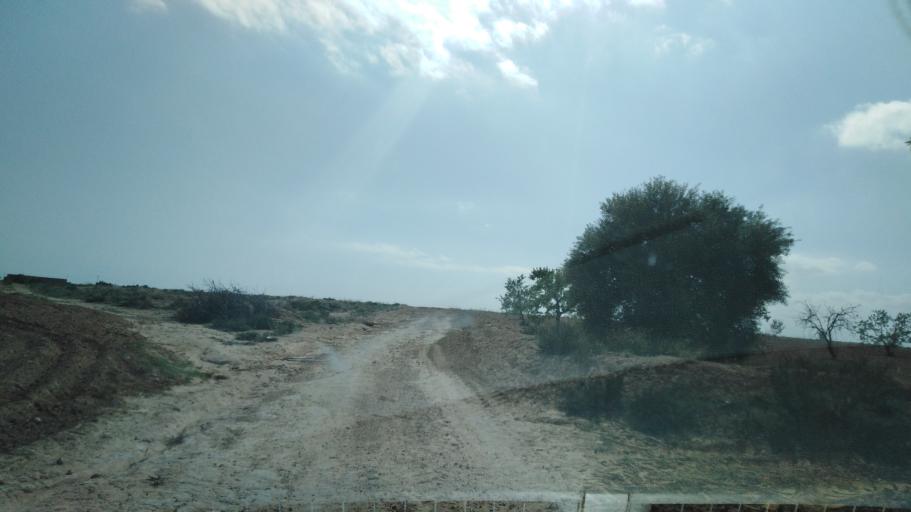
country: TN
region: Safaqis
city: Bi'r `Ali Bin Khalifah
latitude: 34.7994
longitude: 10.3768
